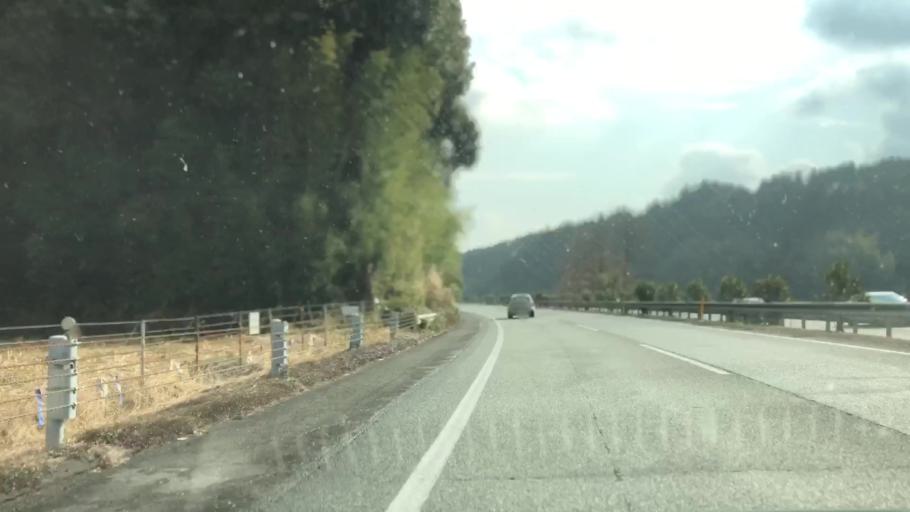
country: JP
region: Kumamoto
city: Yamaga
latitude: 33.0248
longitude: 130.5775
